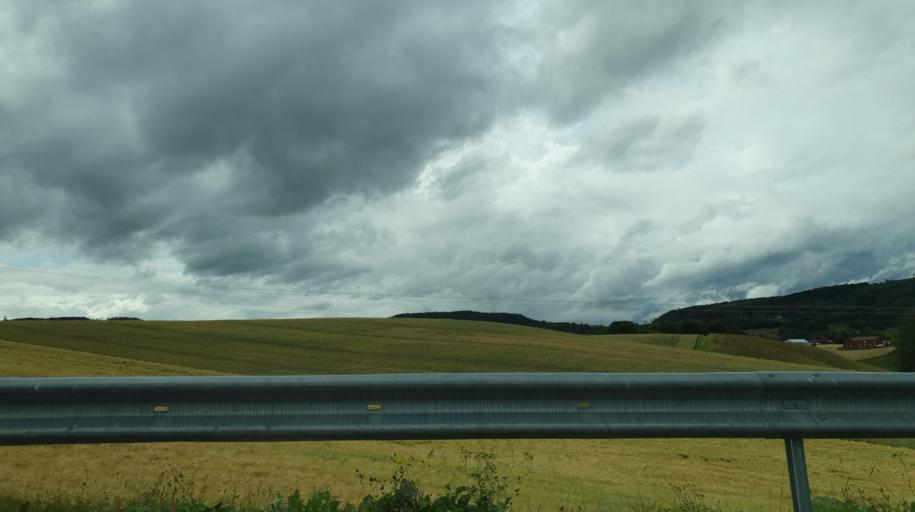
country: NO
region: Nord-Trondelag
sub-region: Stjordal
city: Stjordalshalsen
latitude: 63.4348
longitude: 10.9439
